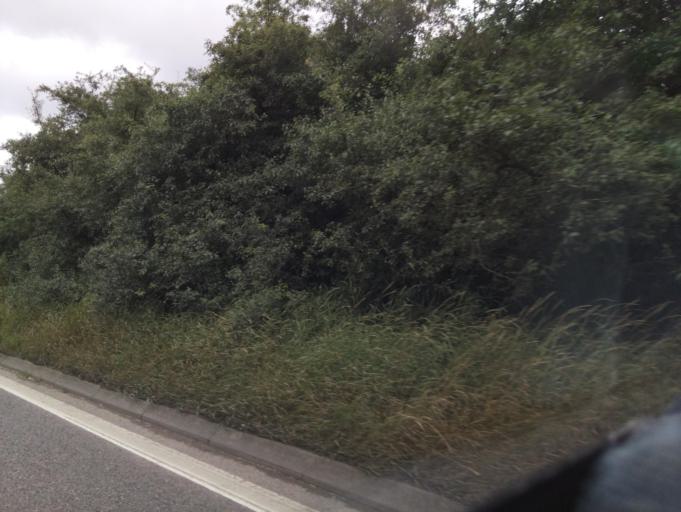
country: GB
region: England
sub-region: Northamptonshire
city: Kettering
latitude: 52.4278
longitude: -0.7315
